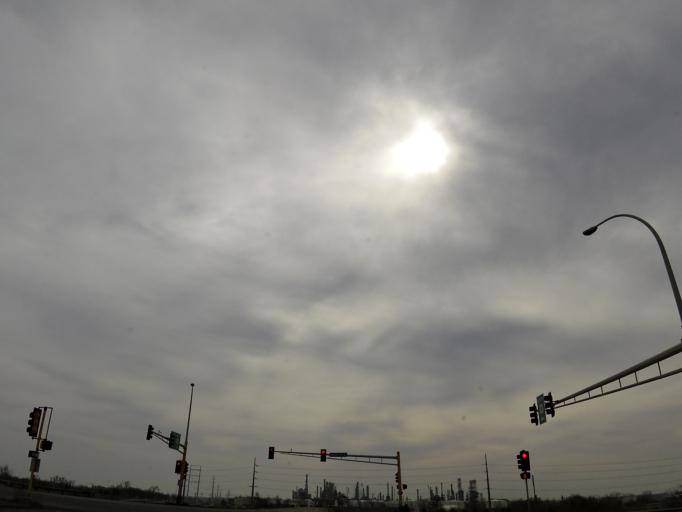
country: US
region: Minnesota
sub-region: Dakota County
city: Inver Grove Heights
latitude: 44.7790
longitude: -93.0359
